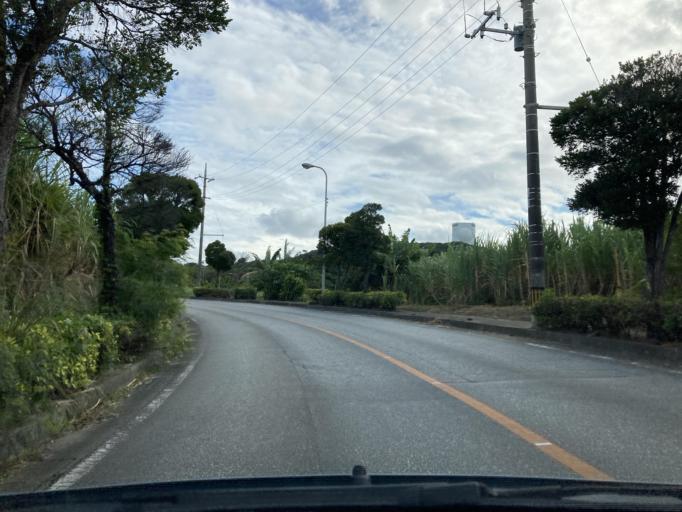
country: JP
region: Okinawa
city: Itoman
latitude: 26.1325
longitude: 127.7058
